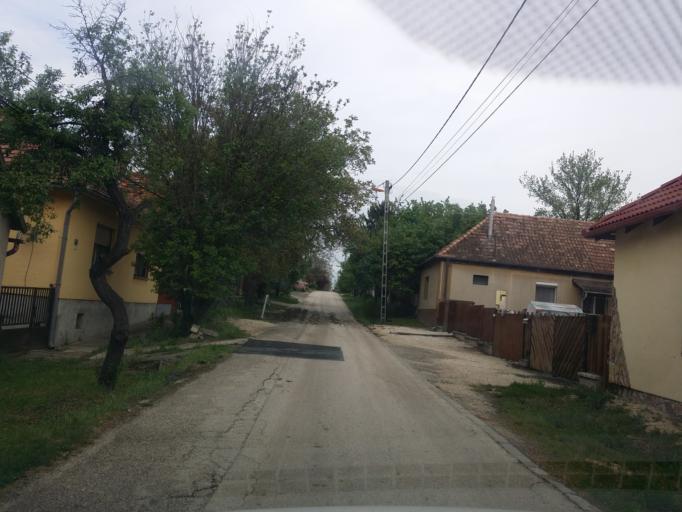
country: HU
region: Pest
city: Biatorbagy
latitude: 47.4744
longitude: 18.8340
